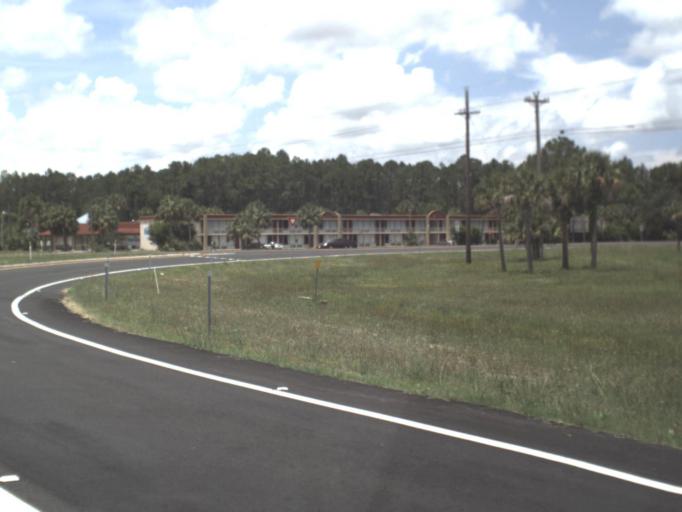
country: US
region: Georgia
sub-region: Camden County
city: Kingsland
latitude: 30.7125
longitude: -81.6723
